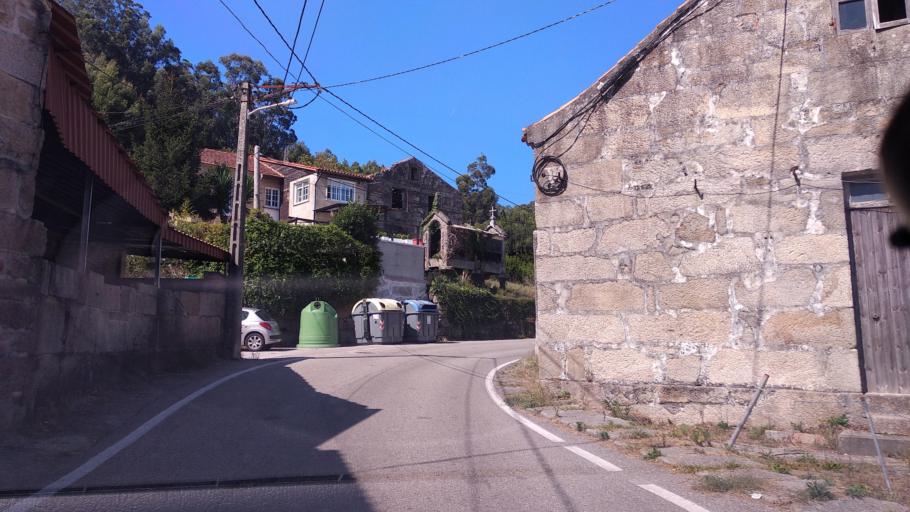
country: ES
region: Galicia
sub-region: Provincia de Pontevedra
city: Moana
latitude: 42.2775
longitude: -8.7591
